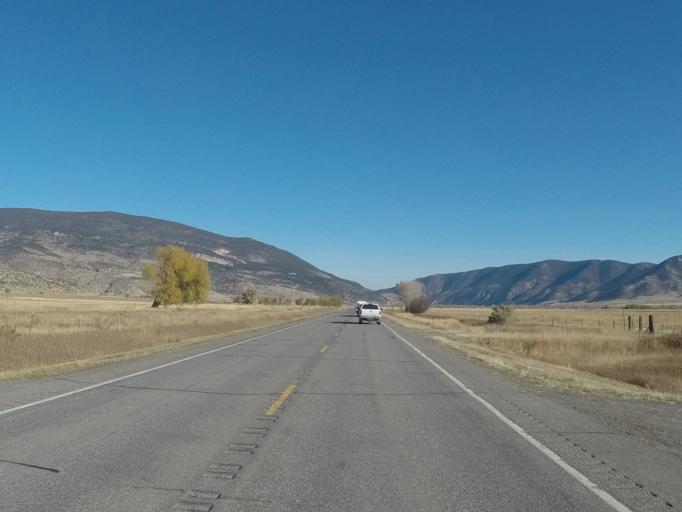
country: US
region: Montana
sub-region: Park County
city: Livingston
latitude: 45.5401
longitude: -110.6015
